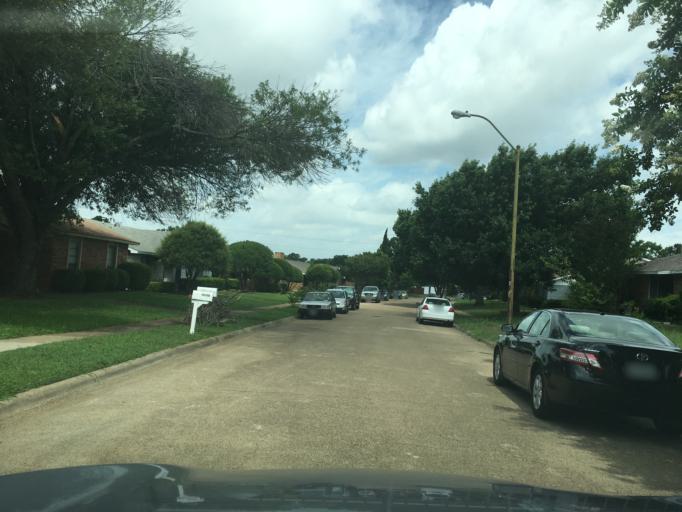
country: US
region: Texas
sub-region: Dallas County
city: Richardson
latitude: 32.9156
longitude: -96.7075
